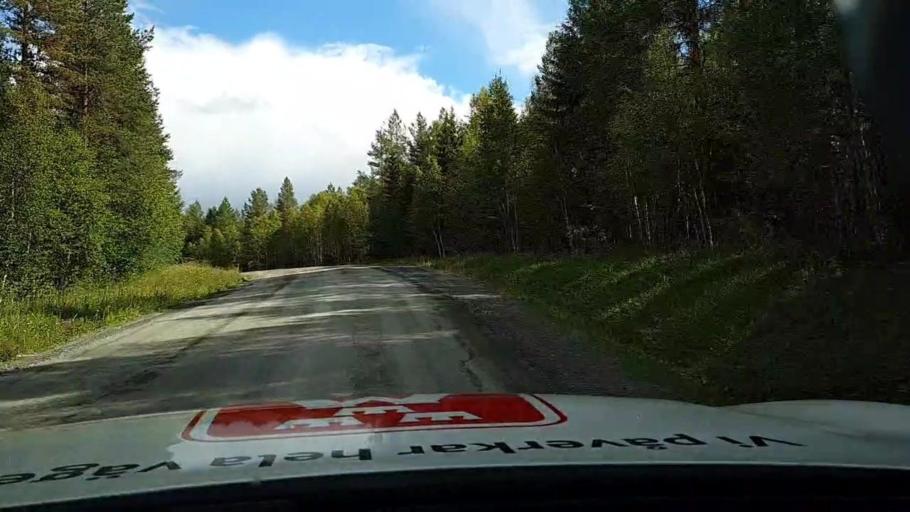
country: SE
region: Jaemtland
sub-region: Krokoms Kommun
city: Valla
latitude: 63.6498
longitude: 13.7862
